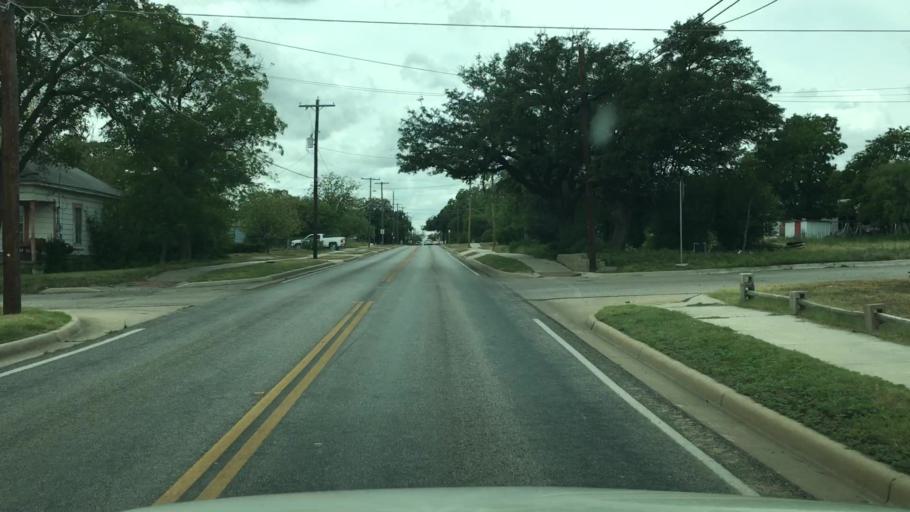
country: US
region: Texas
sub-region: McCulloch County
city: Brady
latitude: 31.1262
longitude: -99.3305
